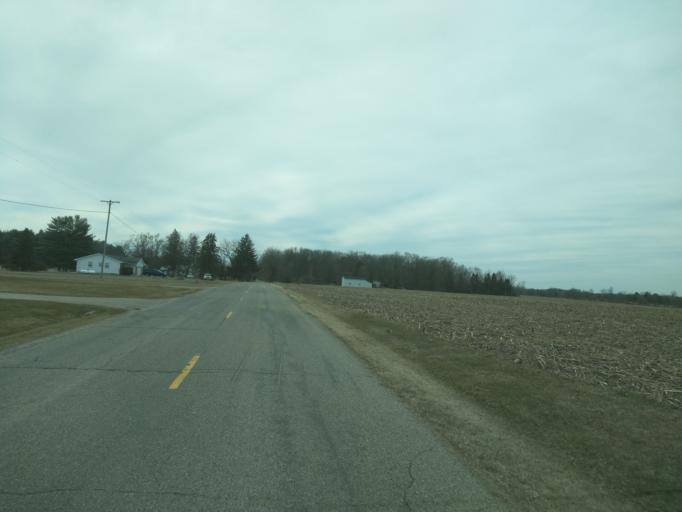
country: US
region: Michigan
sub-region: Ingham County
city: Okemos
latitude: 42.6688
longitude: -84.3726
